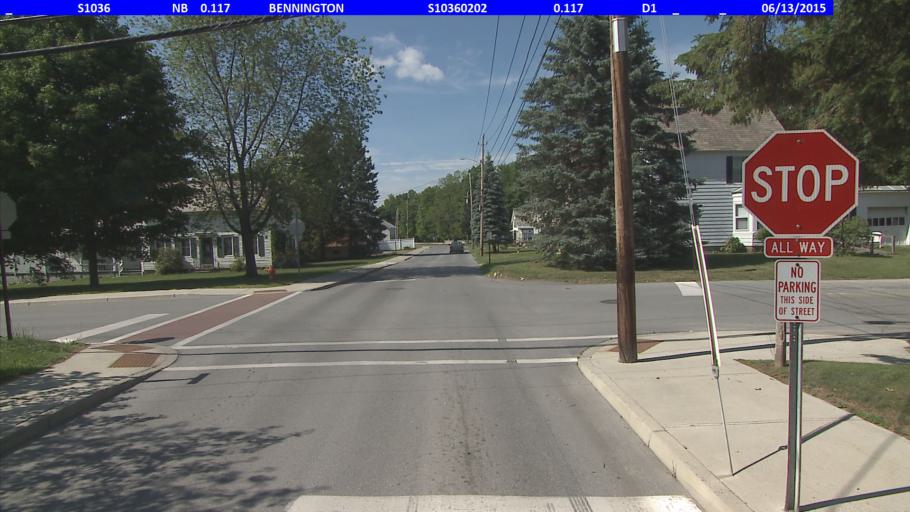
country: US
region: Vermont
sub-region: Bennington County
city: Bennington
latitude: 42.8811
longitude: -73.1808
